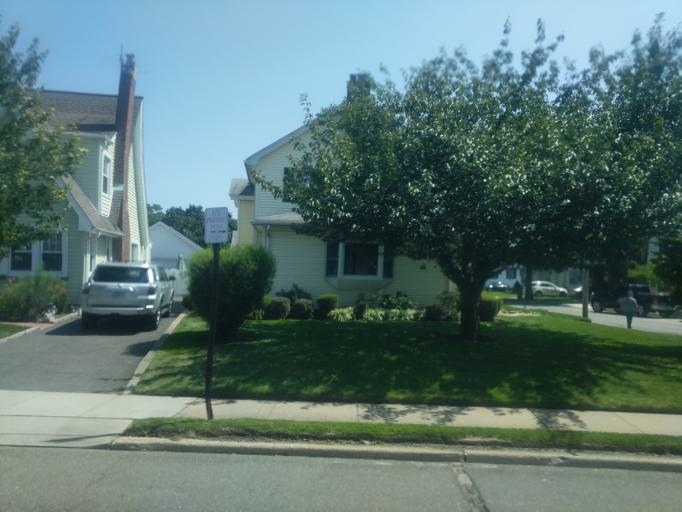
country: US
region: New York
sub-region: Nassau County
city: Malverne
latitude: 40.6682
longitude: -73.6703
